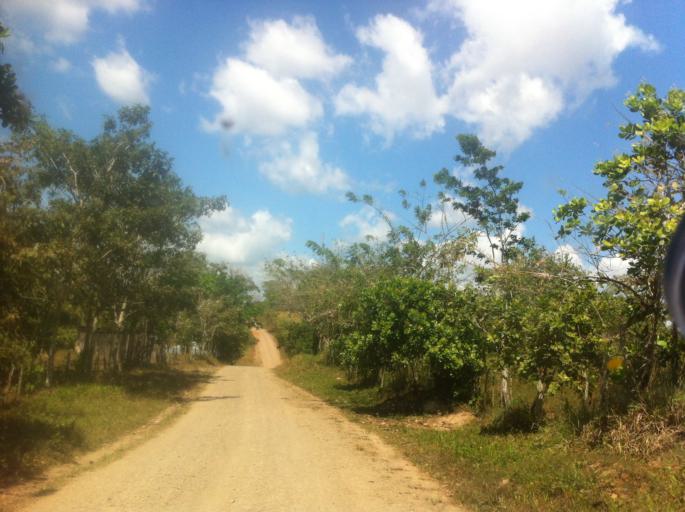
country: CR
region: Alajuela
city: Los Chiles
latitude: 11.2424
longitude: -84.4670
